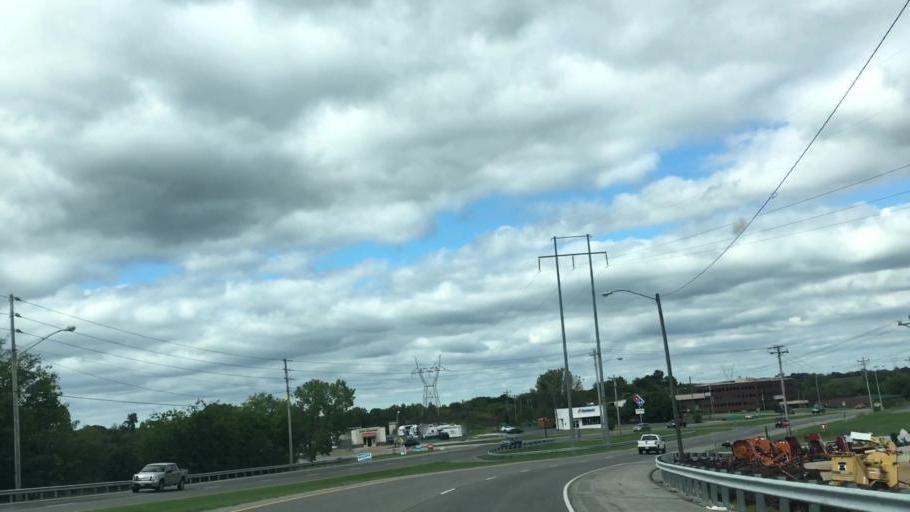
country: US
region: Tennessee
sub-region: Maury County
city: Columbia
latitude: 35.6102
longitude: -87.0691
